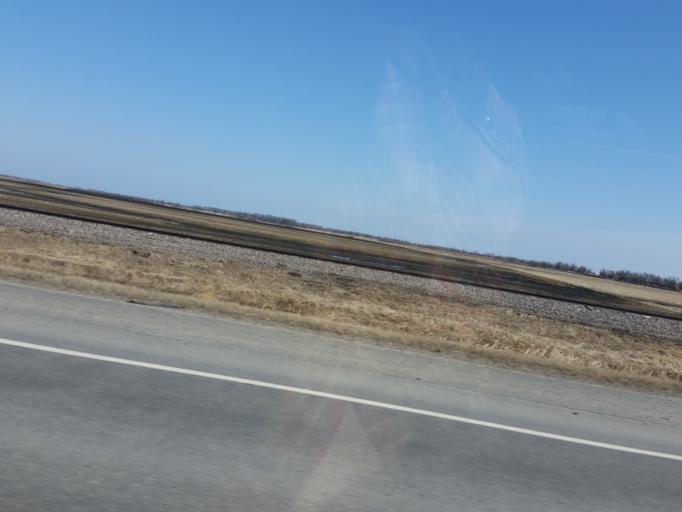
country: US
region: North Dakota
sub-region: Walsh County
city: Grafton
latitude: 48.2761
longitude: -97.3662
